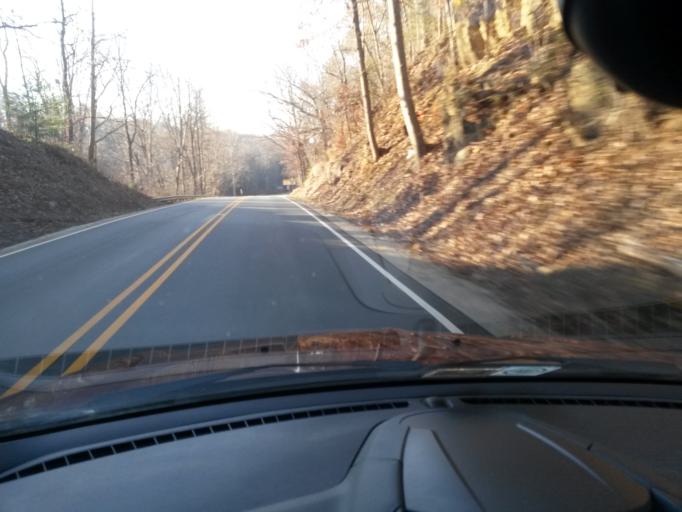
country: US
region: Virginia
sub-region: Amherst County
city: Amherst
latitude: 37.6122
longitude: -79.0819
